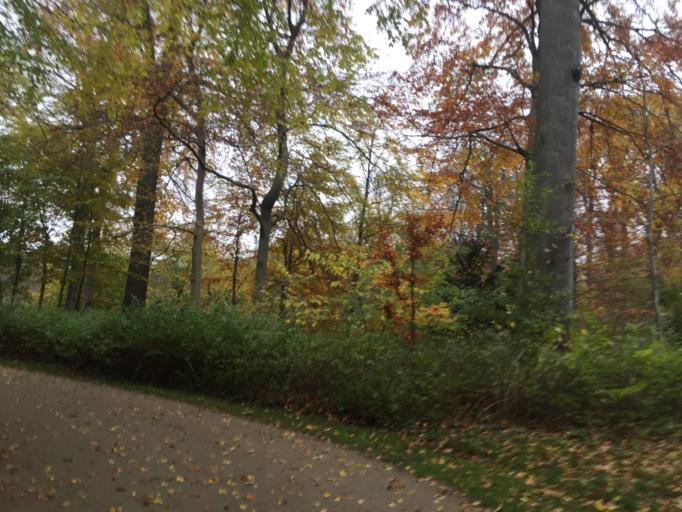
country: DK
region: Capital Region
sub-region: Frederiksberg Kommune
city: Frederiksberg
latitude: 55.6761
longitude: 12.5241
